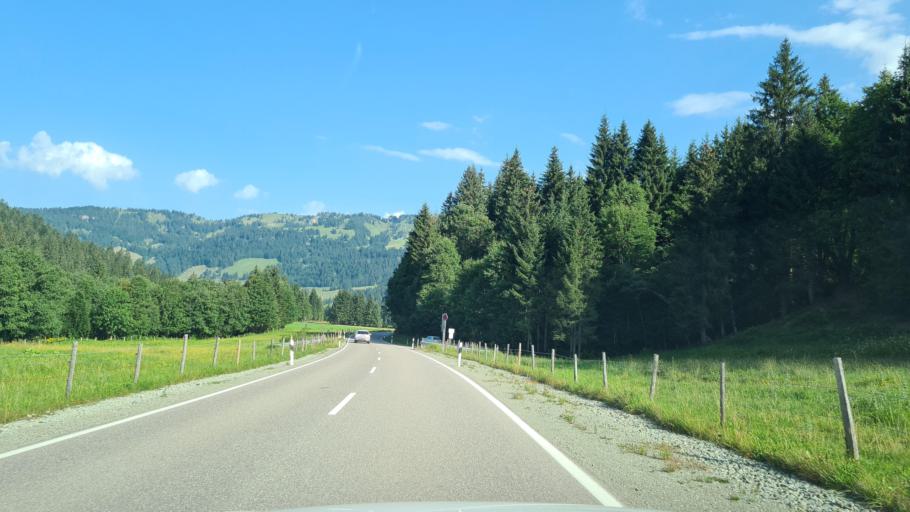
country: DE
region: Bavaria
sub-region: Swabia
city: Balderschwang
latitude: 47.4478
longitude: 10.1352
